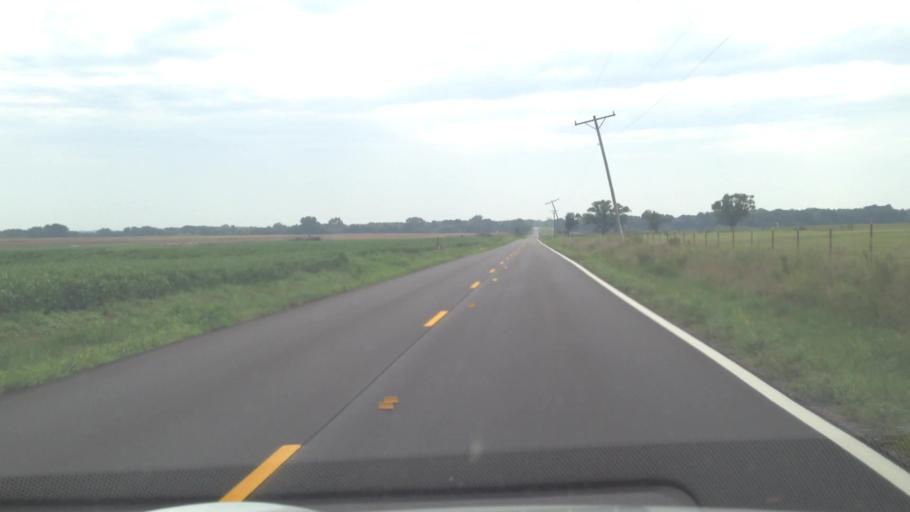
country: US
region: Kansas
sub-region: Crawford County
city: Girard
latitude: 37.6197
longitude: -94.9698
